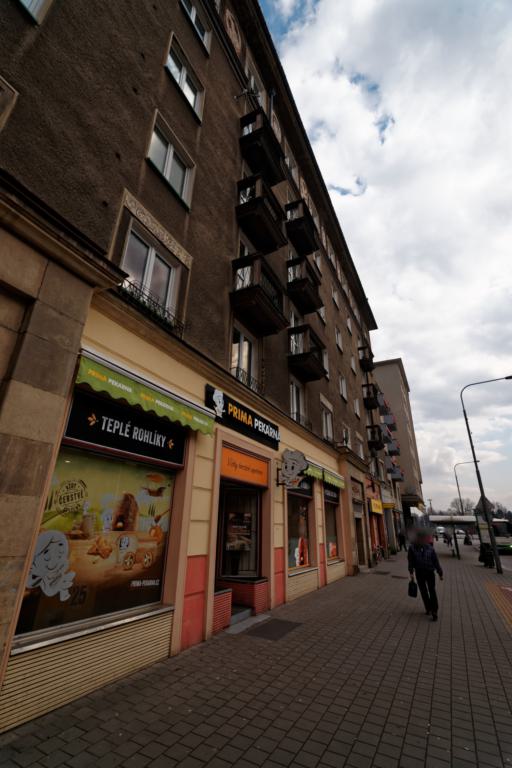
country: CZ
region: Moravskoslezsky
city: Havirov
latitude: 49.7811
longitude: 18.4294
